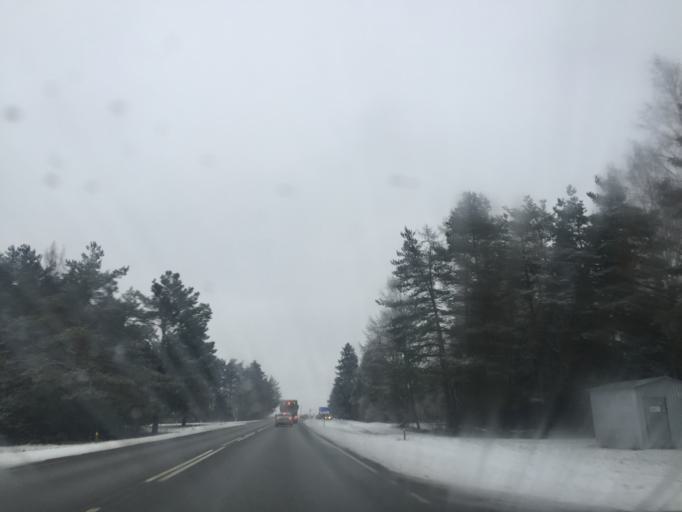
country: EE
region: Laeaene
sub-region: Lihula vald
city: Lihula
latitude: 58.6617
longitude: 23.7296
